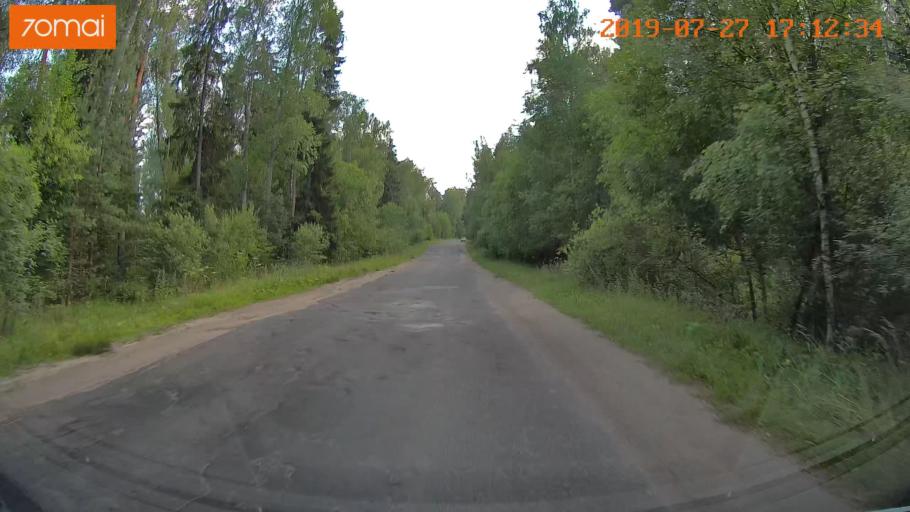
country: RU
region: Ivanovo
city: Novo-Talitsy
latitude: 57.0573
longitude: 40.8605
